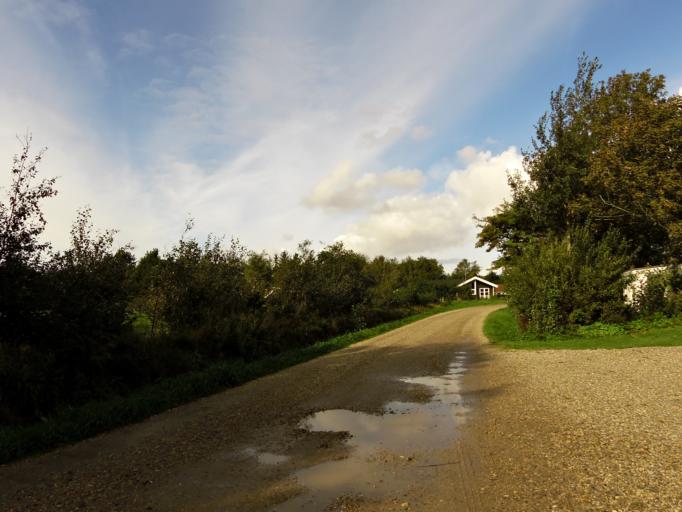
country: DK
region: South Denmark
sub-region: Varde Kommune
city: Oksbol
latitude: 55.5539
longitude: 8.2185
